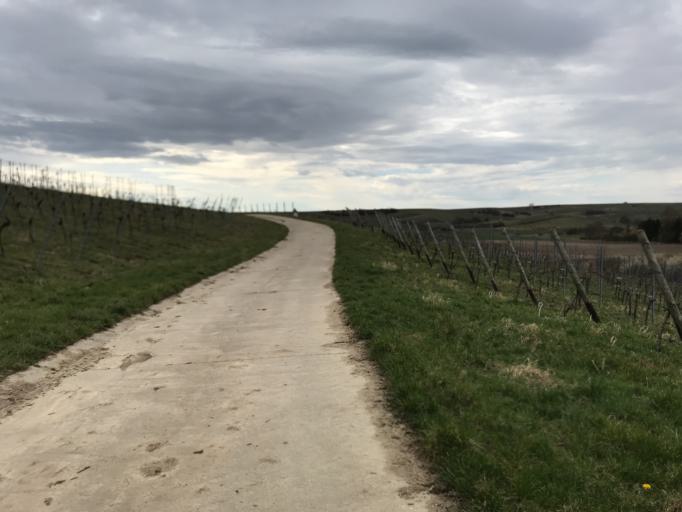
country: DE
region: Rheinland-Pfalz
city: Stadecken-Elsheim
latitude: 49.8936
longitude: 8.1290
